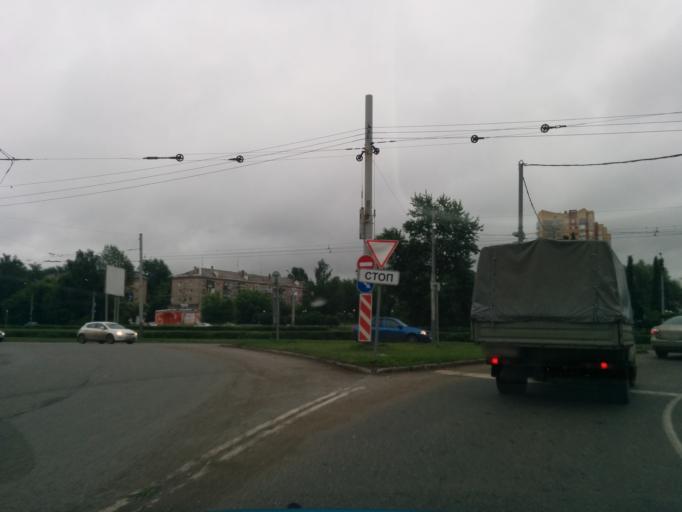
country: RU
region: Perm
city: Perm
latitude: 57.9897
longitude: 56.1887
